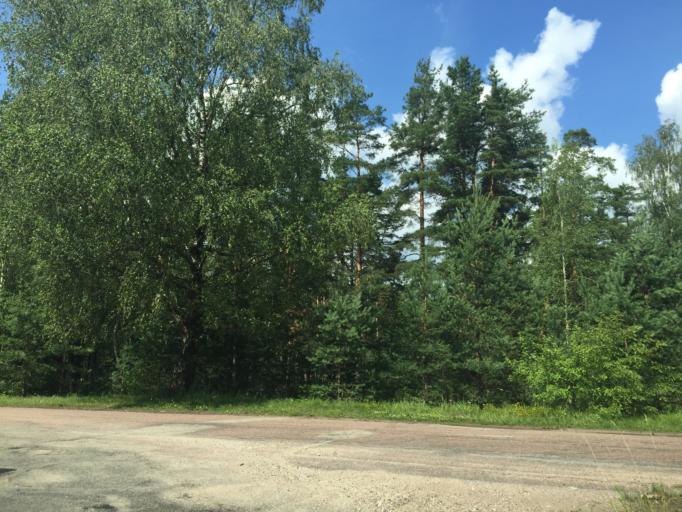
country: LV
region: Olaine
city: Olaine
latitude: 56.8089
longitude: 23.9962
